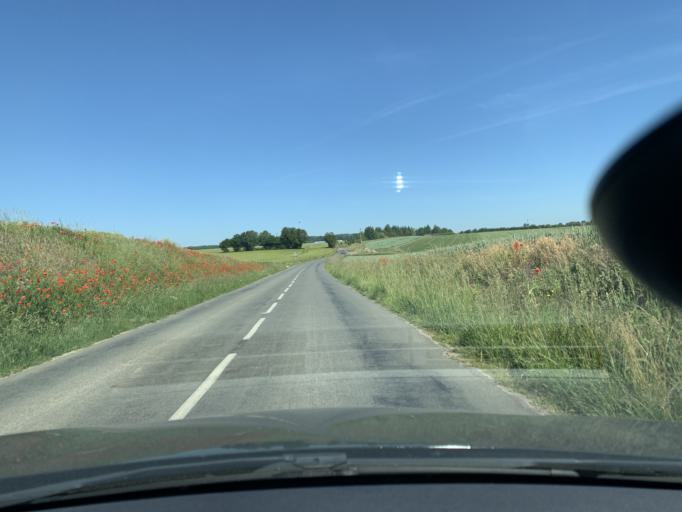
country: FR
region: Nord-Pas-de-Calais
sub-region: Departement du Nord
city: Fontaine-Notre-Dame
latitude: 50.1532
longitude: 3.1661
